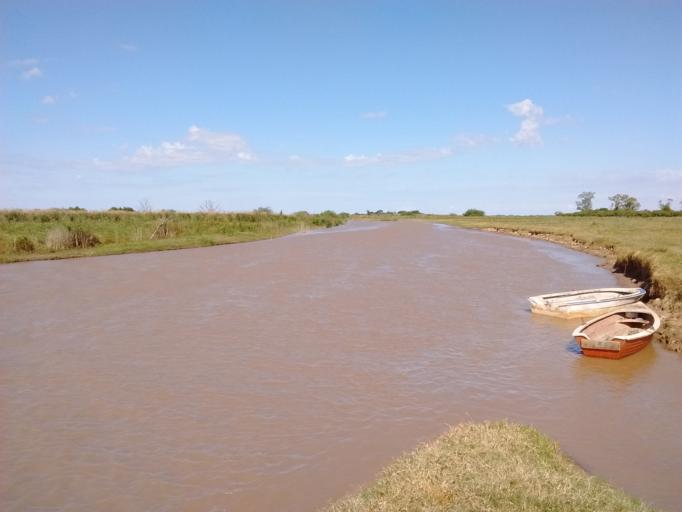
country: AR
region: Santa Fe
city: Coronda
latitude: -32.2492
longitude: -60.9104
